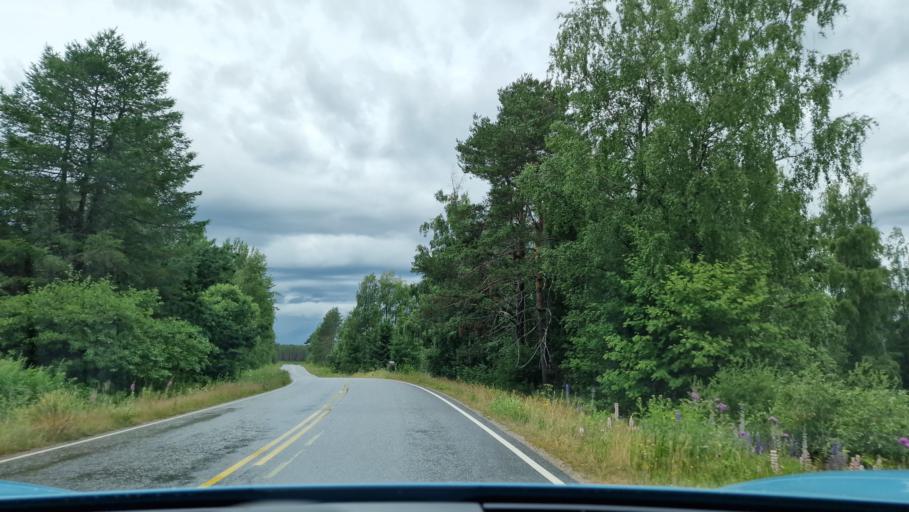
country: FI
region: Central Finland
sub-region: Saarijaervi-Viitasaari
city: Pylkoenmaeki
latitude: 62.6808
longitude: 24.4985
